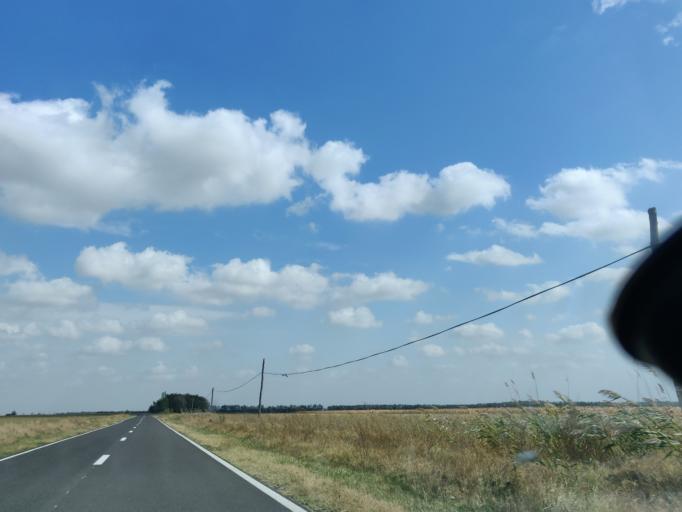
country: RO
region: Vrancea
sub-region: Comuna Maicanesti
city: Ramniceni
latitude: 45.4733
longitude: 27.4312
